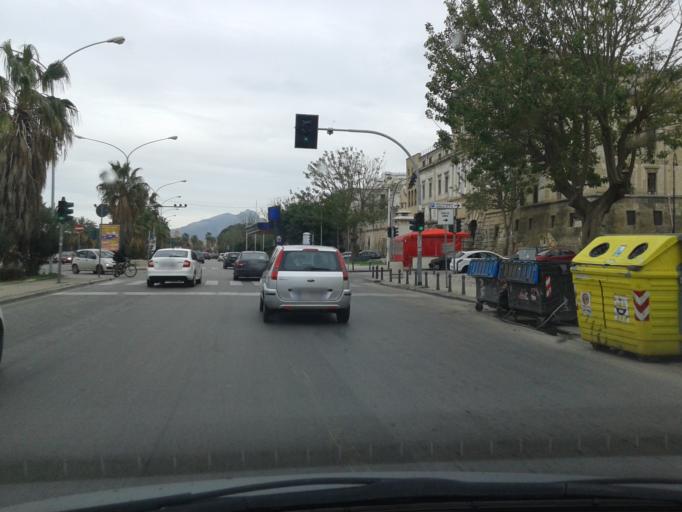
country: IT
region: Sicily
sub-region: Palermo
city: Palermo
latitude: 38.1170
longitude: 13.3736
